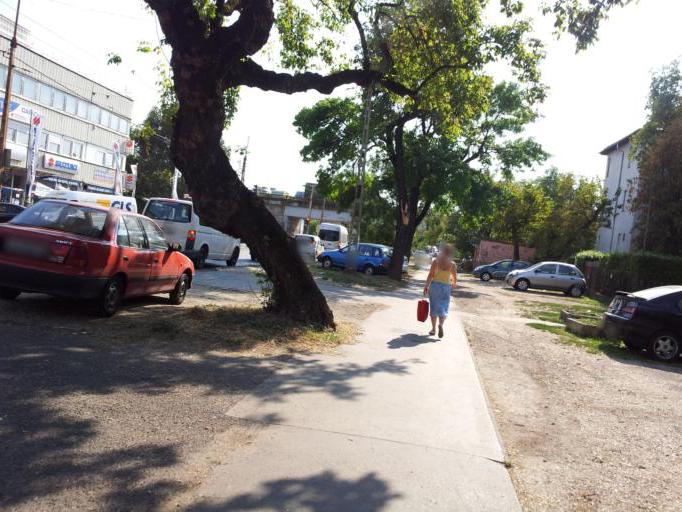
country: HU
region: Budapest
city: Budapest XIV. keruelet
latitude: 47.5078
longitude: 19.1076
